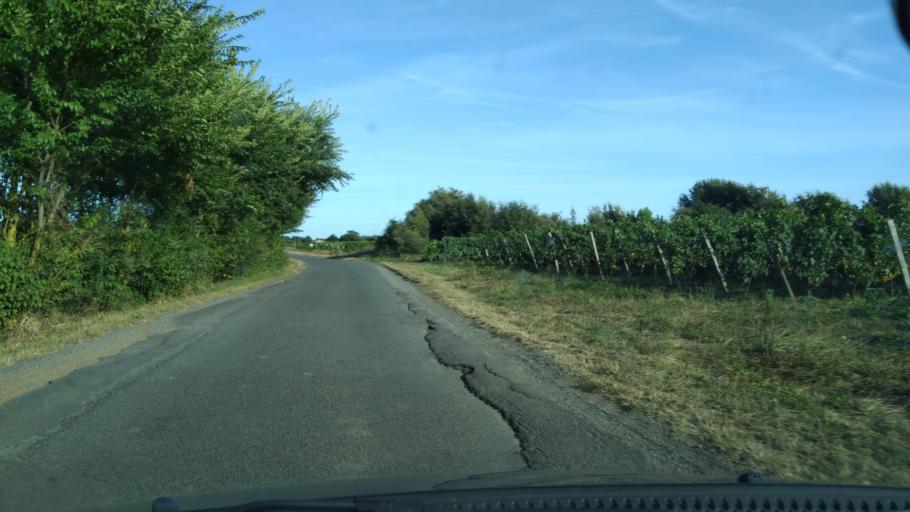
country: FR
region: Poitou-Charentes
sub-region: Departement de la Charente-Maritime
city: Dolus-d'Oleron
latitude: 45.9440
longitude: -1.3433
